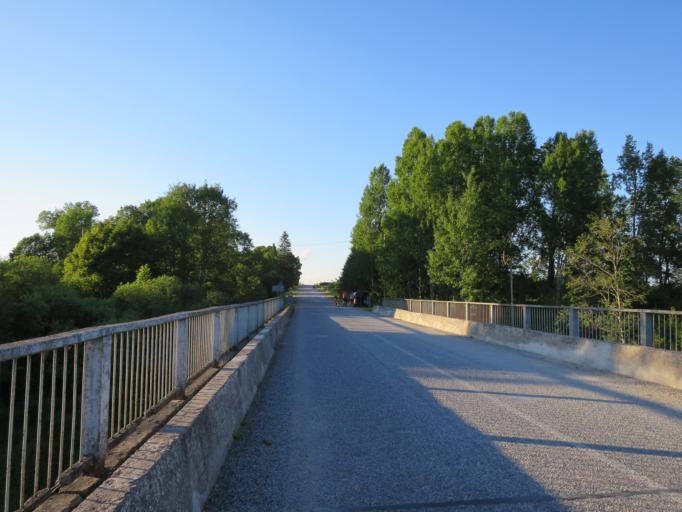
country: LV
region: Rucavas
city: Rucava
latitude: 56.3322
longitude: 21.3091
